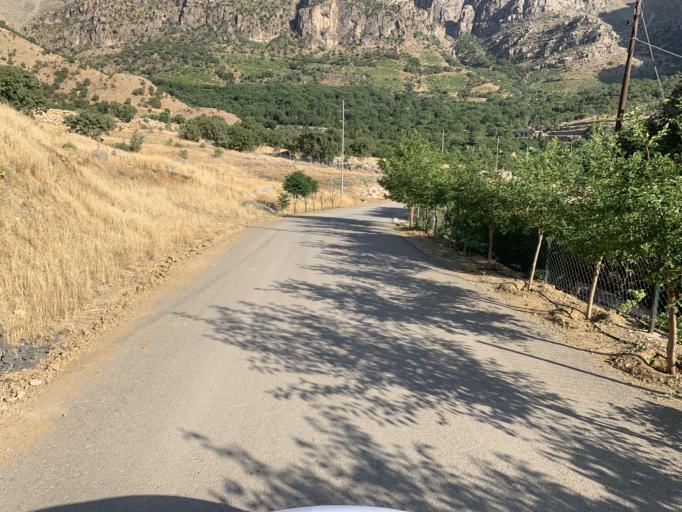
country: IQ
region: As Sulaymaniyah
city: Qeladize
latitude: 35.9909
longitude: 45.1997
